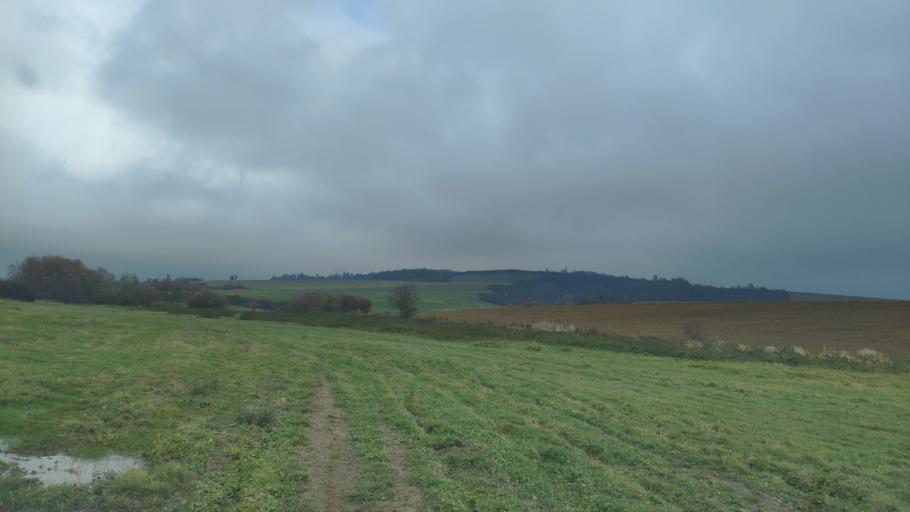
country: SK
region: Presovsky
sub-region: Okres Presov
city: Presov
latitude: 49.0155
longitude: 21.2001
